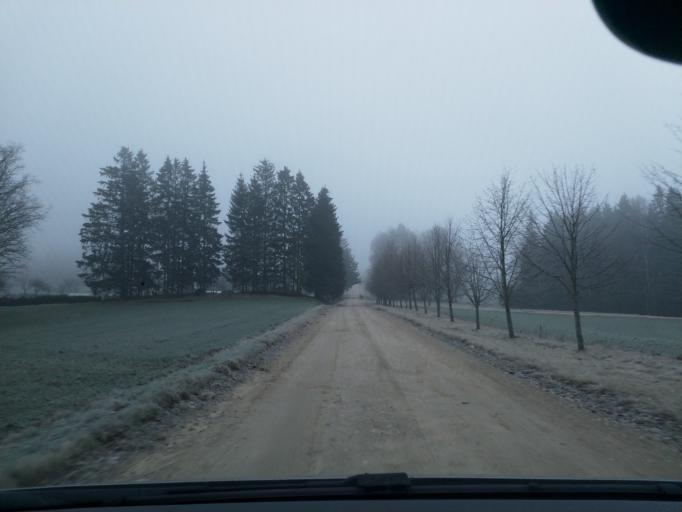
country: LV
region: Kuldigas Rajons
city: Kuldiga
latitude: 56.8474
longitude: 21.9307
